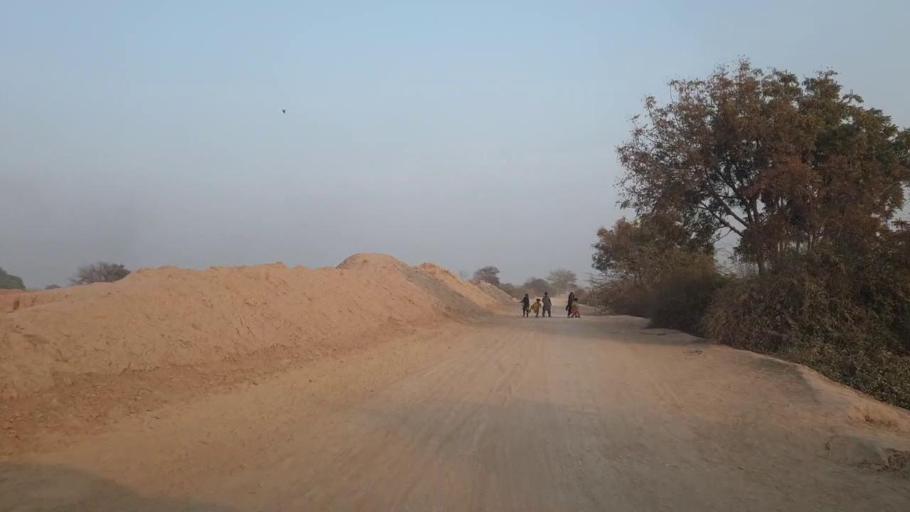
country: PK
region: Sindh
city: Bhit Shah
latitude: 25.7818
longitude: 68.4597
